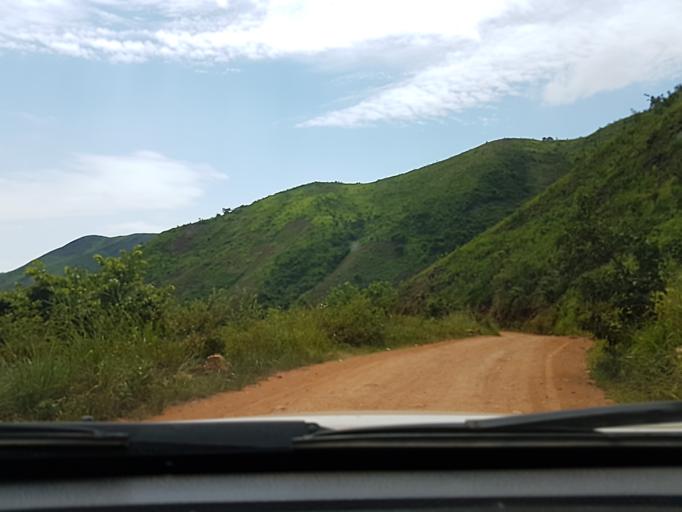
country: RW
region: Western Province
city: Cyangugu
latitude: -2.7069
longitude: 28.9431
